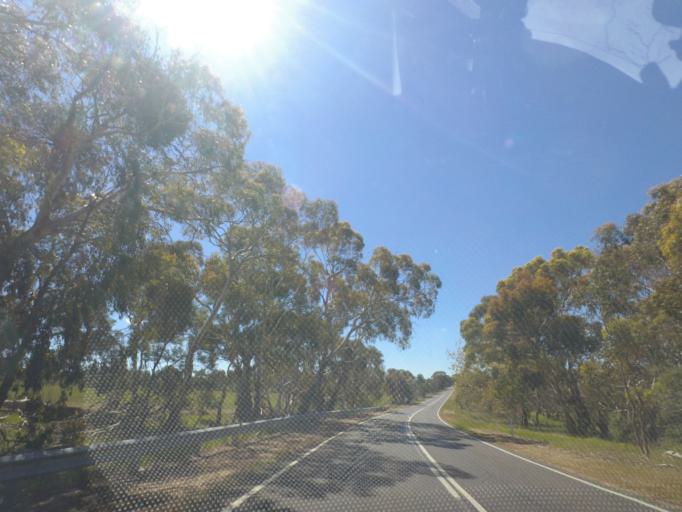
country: AU
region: Victoria
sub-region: Hume
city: Sunbury
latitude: -37.1319
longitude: 144.7672
